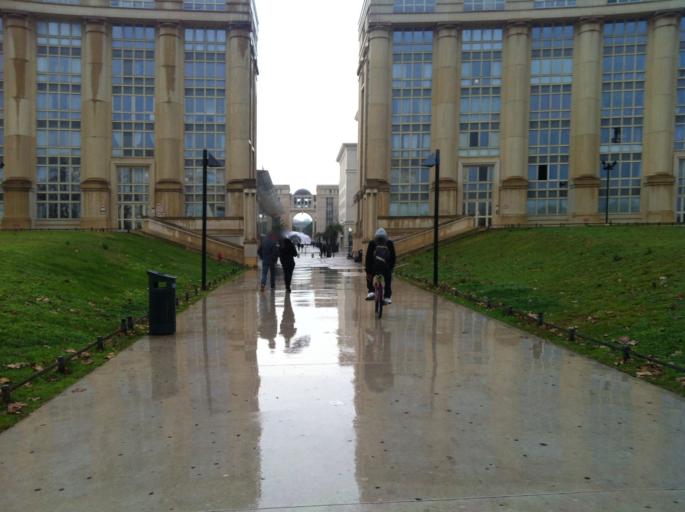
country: FR
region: Languedoc-Roussillon
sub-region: Departement de l'Herault
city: Montpellier
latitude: 43.6077
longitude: 3.8950
